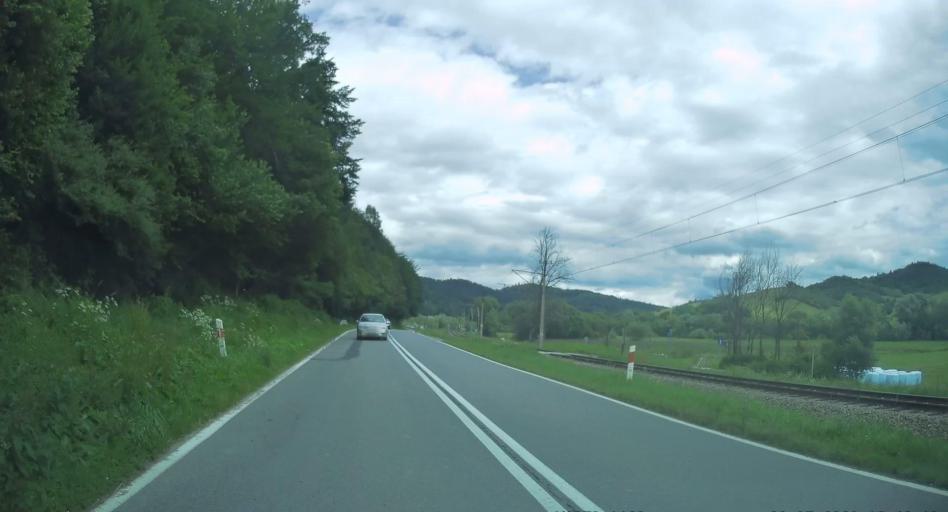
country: PL
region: Lesser Poland Voivodeship
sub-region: Powiat nowosadecki
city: Muszyna
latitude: 49.3421
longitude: 20.8451
